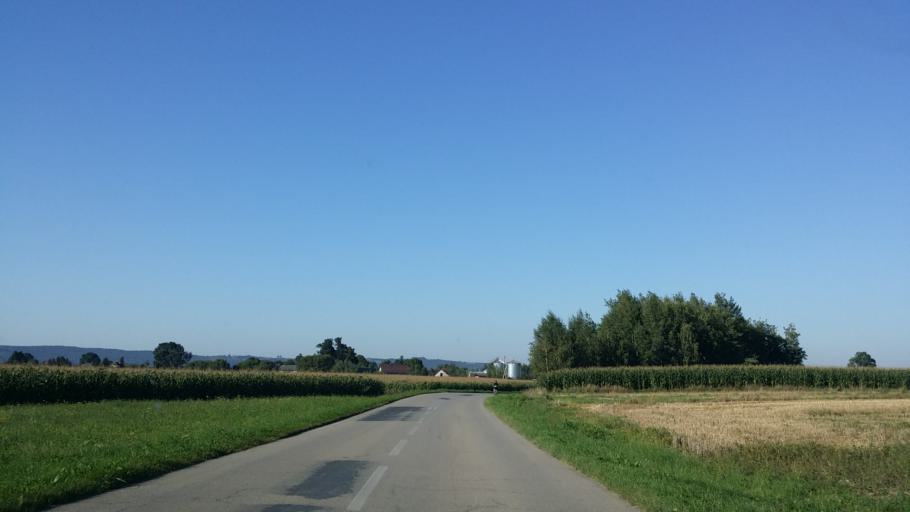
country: PL
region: Lesser Poland Voivodeship
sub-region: Powiat oswiecimski
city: Zator
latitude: 50.0213
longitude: 19.4538
